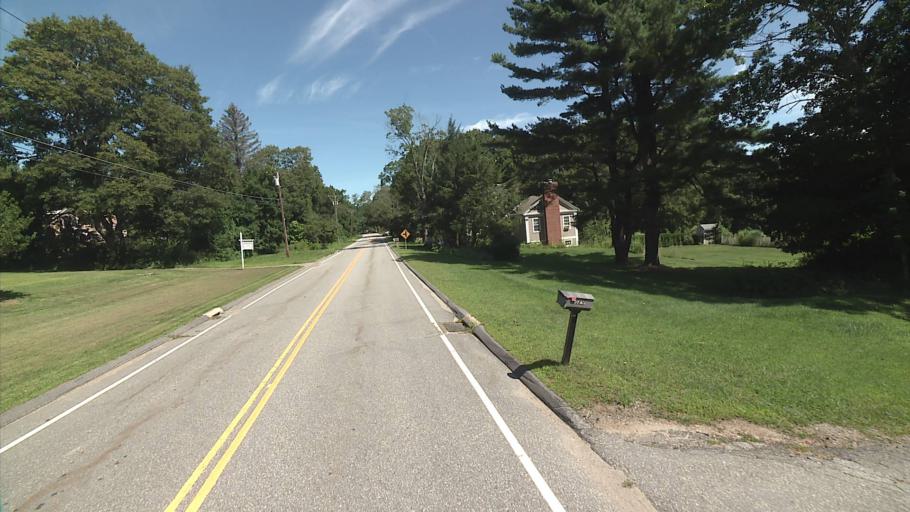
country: US
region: Connecticut
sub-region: Windham County
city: Windham
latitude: 41.7795
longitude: -72.0553
